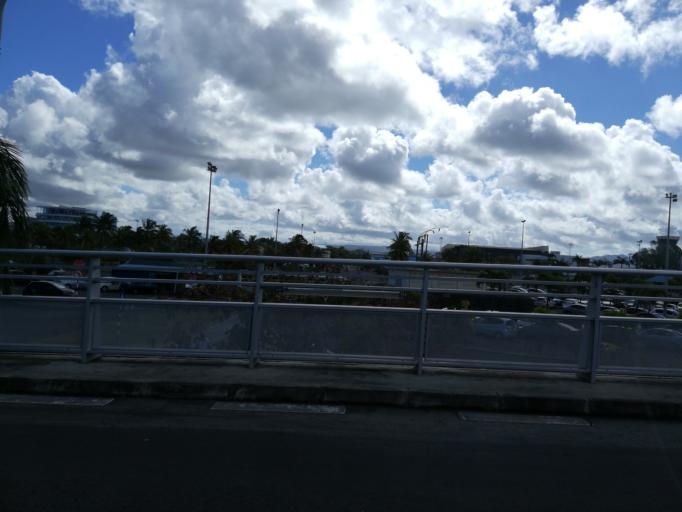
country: MU
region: Grand Port
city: Plaine Magnien
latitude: -20.4334
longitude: 57.6772
